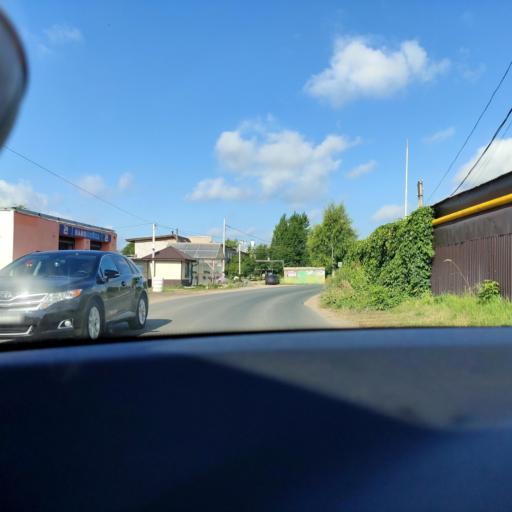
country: RU
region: Samara
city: Volzhskiy
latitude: 53.4330
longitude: 50.1016
